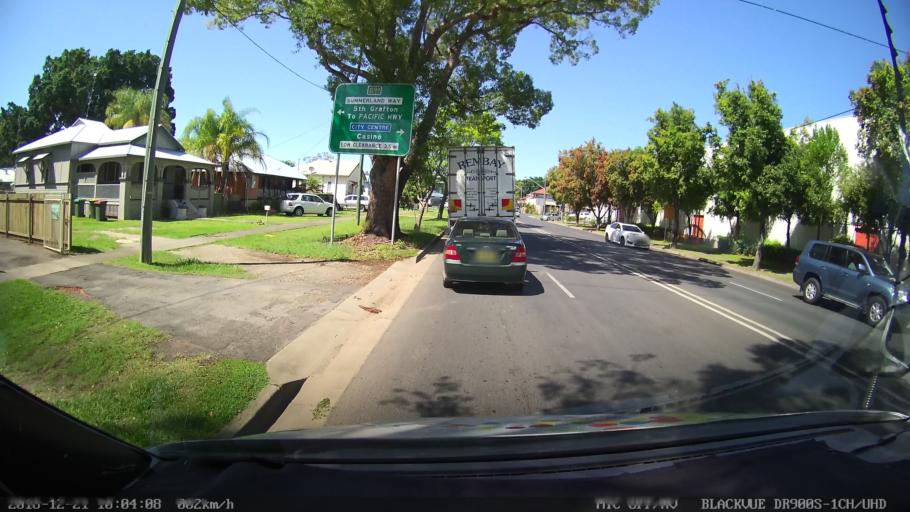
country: AU
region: New South Wales
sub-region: Clarence Valley
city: Grafton
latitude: -29.6925
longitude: 152.9376
